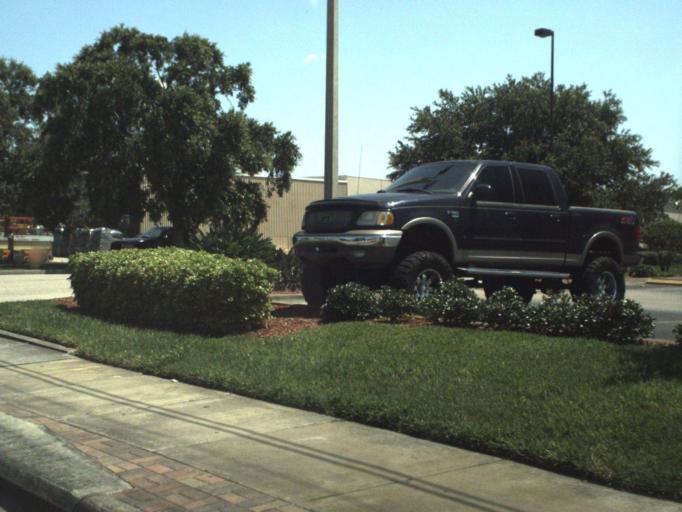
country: US
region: Florida
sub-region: Brevard County
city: Rockledge
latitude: 28.3580
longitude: -80.7001
